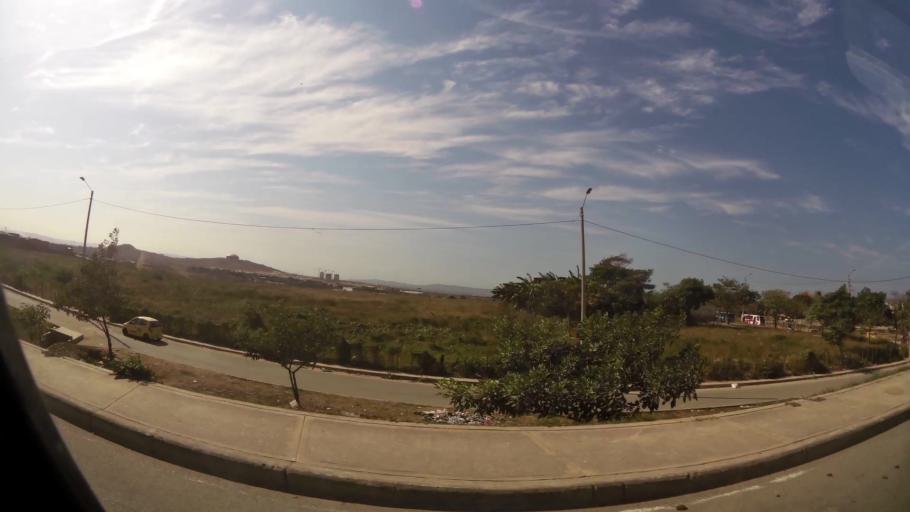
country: CO
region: Atlantico
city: Soledad
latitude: 10.9218
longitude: -74.8171
